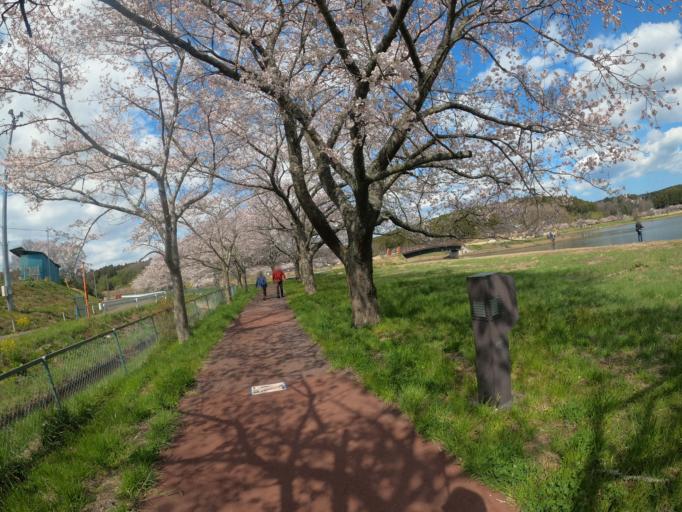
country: JP
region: Miyagi
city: Wakuya
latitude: 38.6188
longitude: 141.2324
